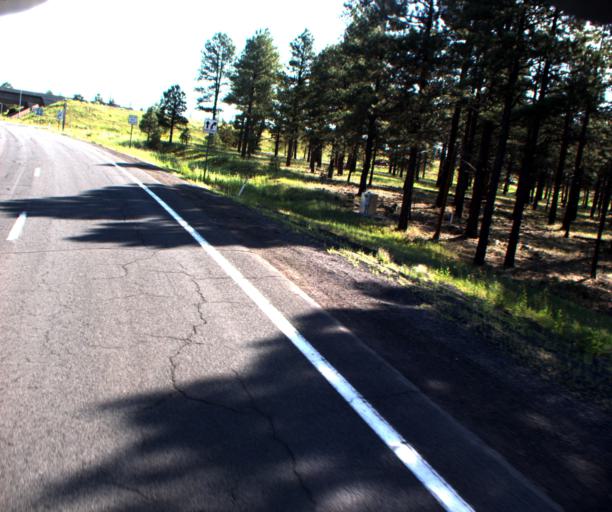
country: US
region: Arizona
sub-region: Coconino County
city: Williams
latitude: 35.2589
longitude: -112.1522
